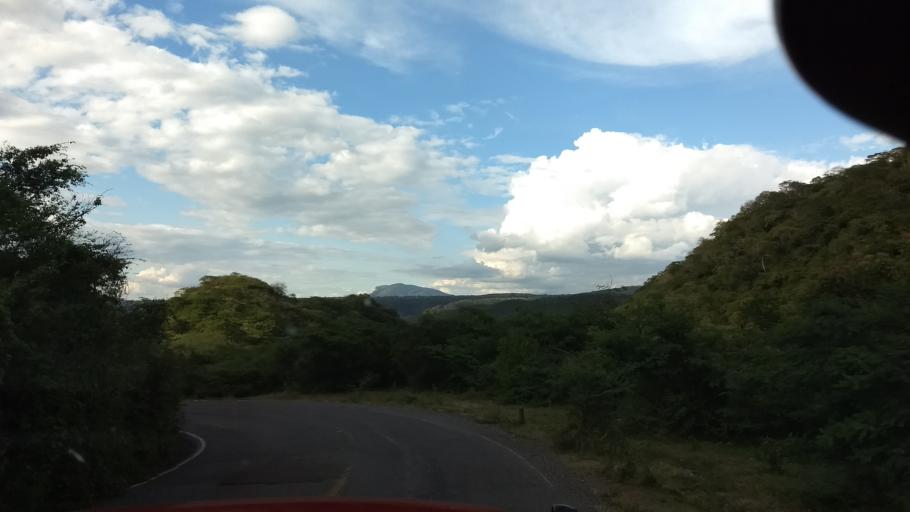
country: MX
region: Colima
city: Suchitlan
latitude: 19.4528
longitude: -103.8209
